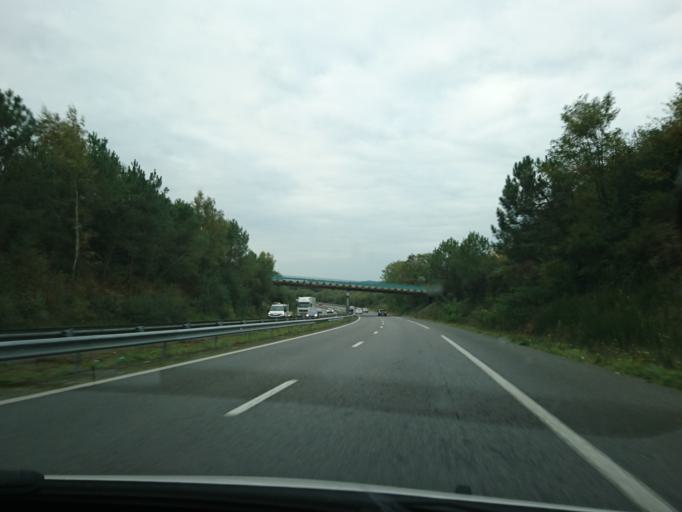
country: FR
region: Brittany
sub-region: Departement du Morbihan
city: Nivillac
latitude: 47.5281
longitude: -2.2851
